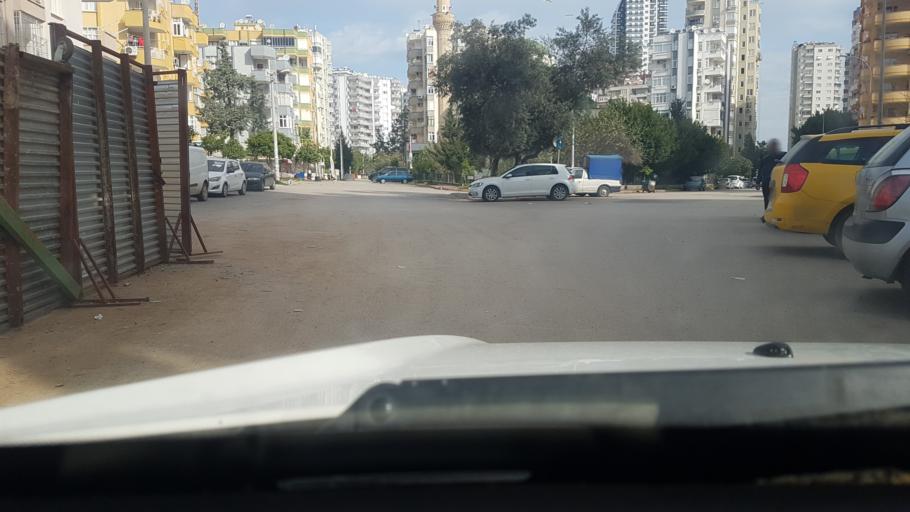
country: TR
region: Adana
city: Adana
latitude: 37.0438
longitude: 35.3025
